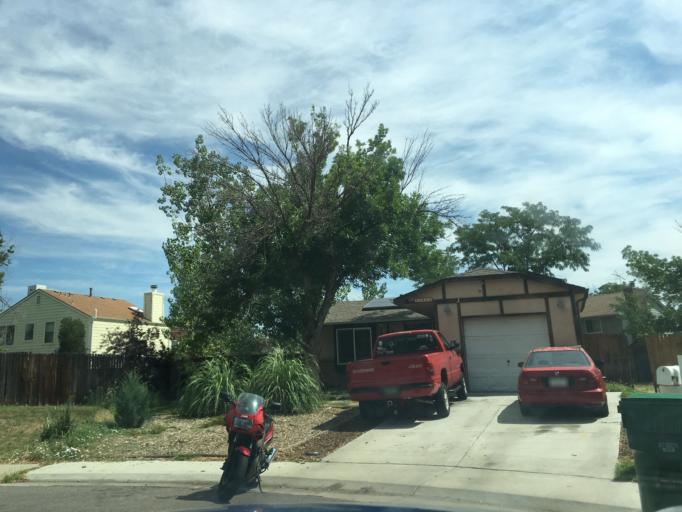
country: US
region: Colorado
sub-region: Adams County
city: Aurora
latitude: 39.7163
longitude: -104.8576
